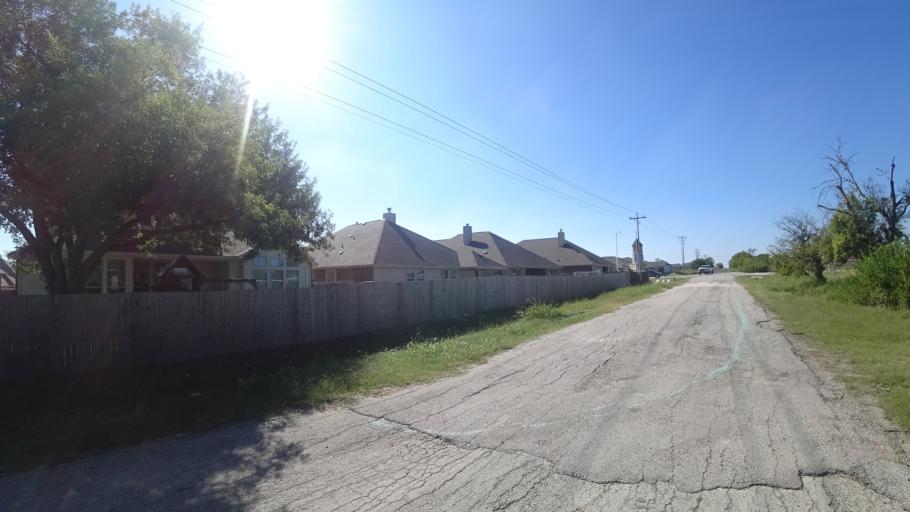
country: US
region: Texas
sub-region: Travis County
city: Manor
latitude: 30.3559
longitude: -97.5997
